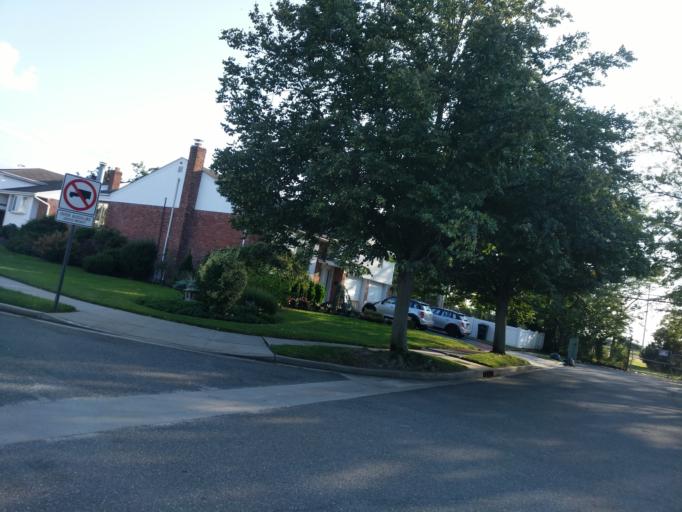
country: US
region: New York
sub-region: Nassau County
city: South Valley Stream
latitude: 40.6485
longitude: -73.7365
